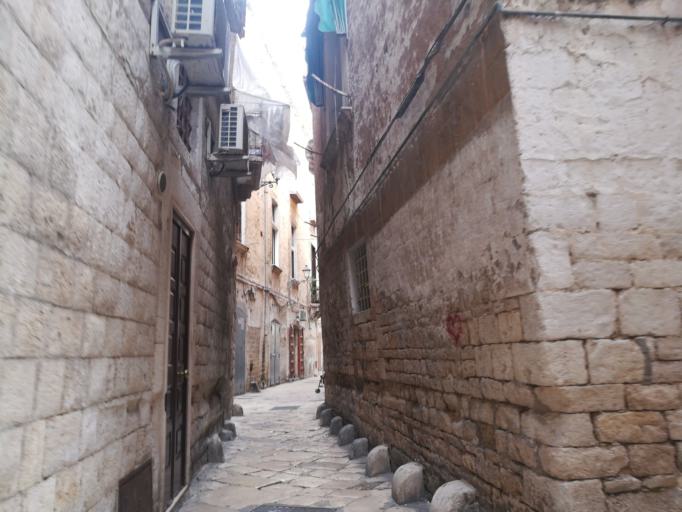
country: IT
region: Apulia
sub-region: Provincia di Bari
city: Bari
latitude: 41.1288
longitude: 16.8704
